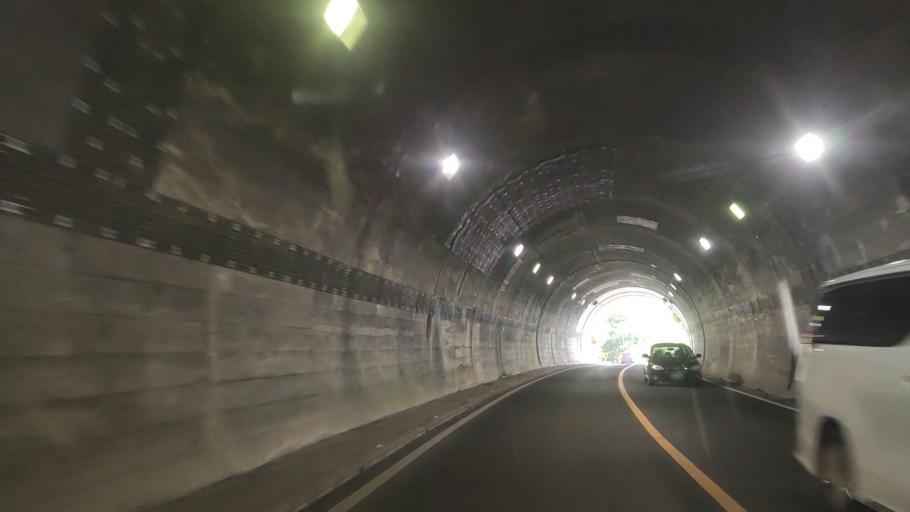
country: JP
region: Tottori
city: Tottori
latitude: 35.5312
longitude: 134.2295
